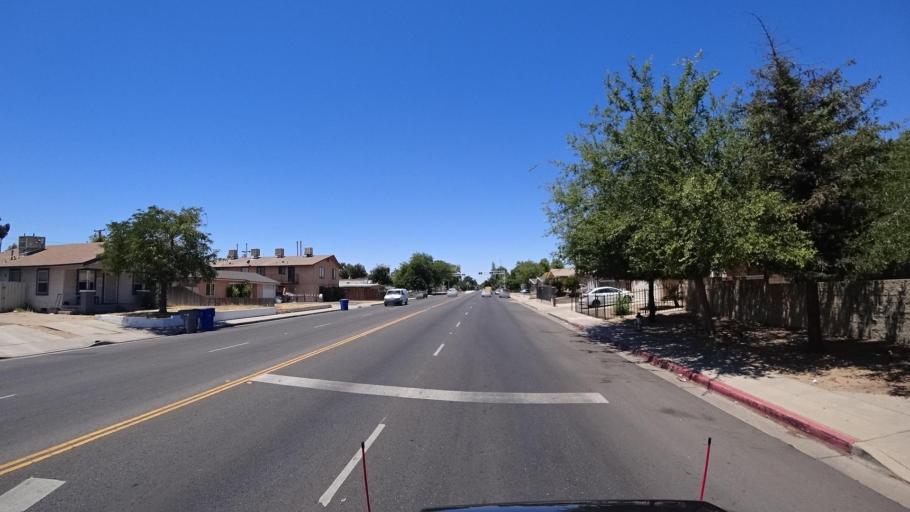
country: US
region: California
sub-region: Fresno County
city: Fresno
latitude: 36.7723
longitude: -119.7953
